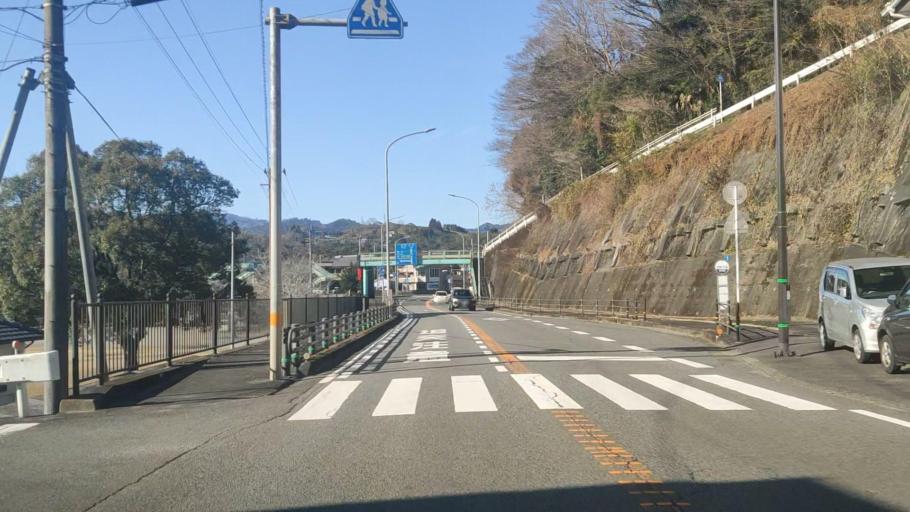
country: JP
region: Oita
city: Oita
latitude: 33.0708
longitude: 131.6395
